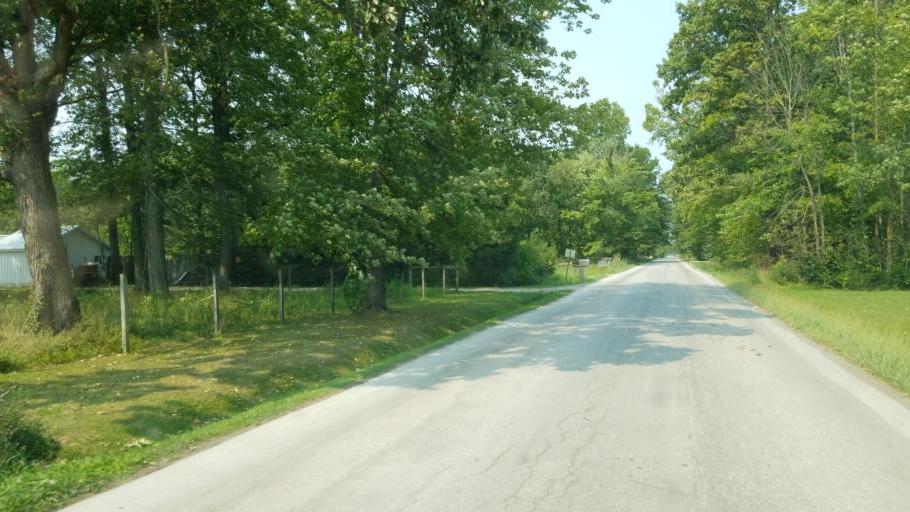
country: US
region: Ohio
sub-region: Geauga County
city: Middlefield
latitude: 41.5011
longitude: -81.0031
